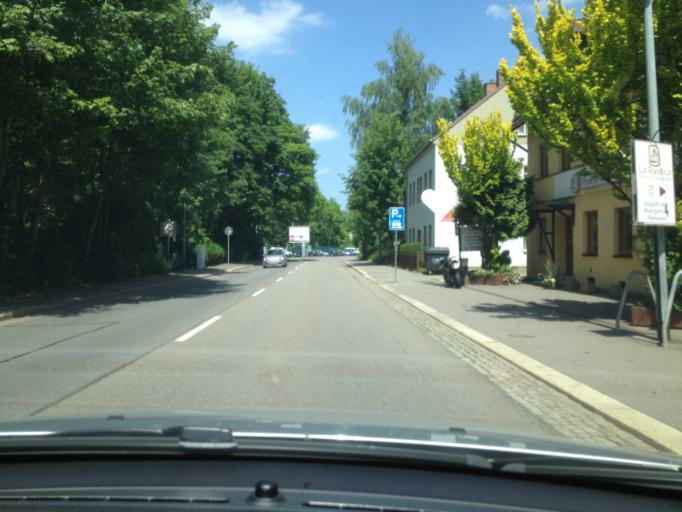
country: DE
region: Saxony
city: Burkhardtsdorf
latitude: 50.7823
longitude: 12.9251
